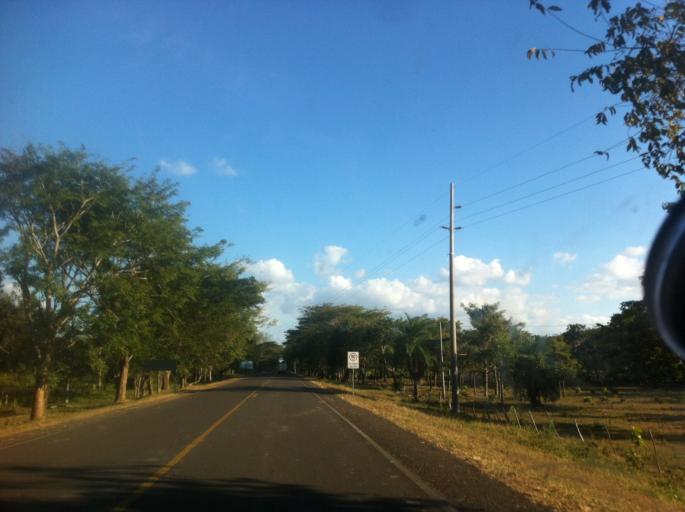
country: NI
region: Rio San Juan
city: Morrito
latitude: 11.6968
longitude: -84.9428
